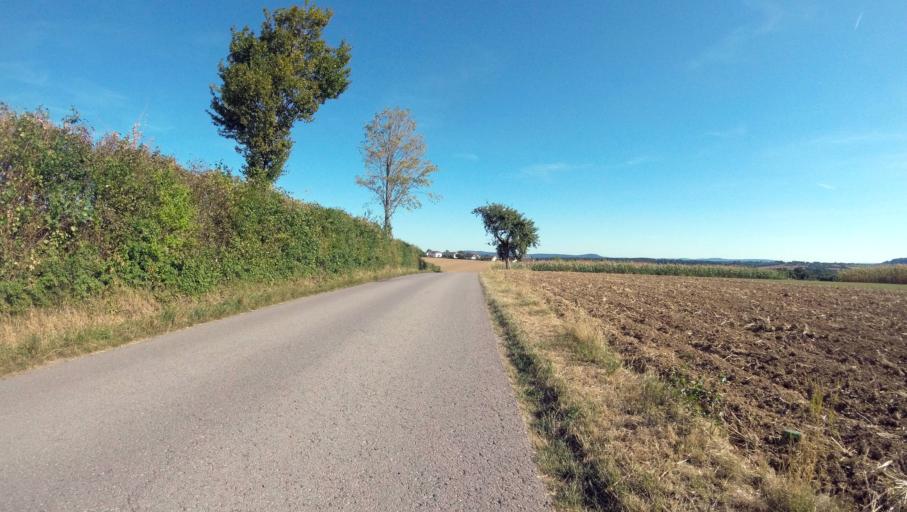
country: DE
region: Baden-Wuerttemberg
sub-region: Regierungsbezirk Stuttgart
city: Kirchberg an der Murr
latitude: 48.9498
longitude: 9.3380
